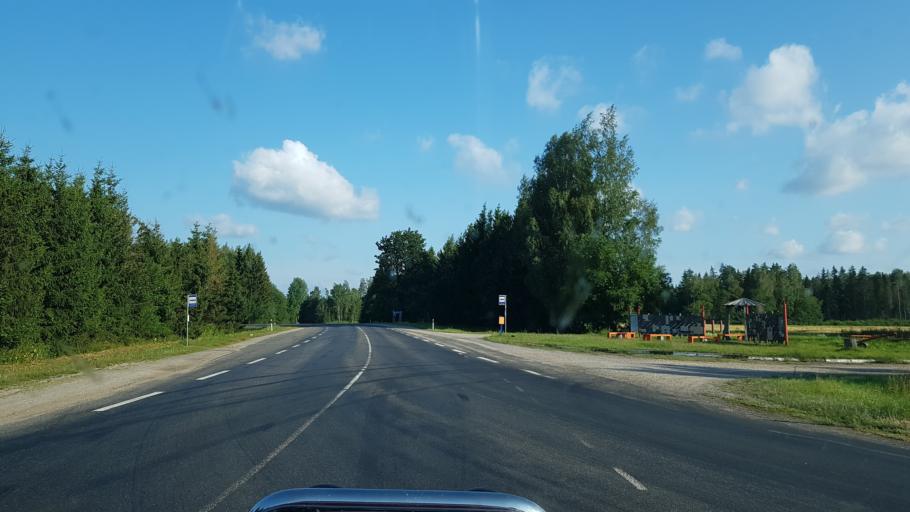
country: EE
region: Polvamaa
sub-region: Polva linn
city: Polva
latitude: 58.0009
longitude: 26.9290
